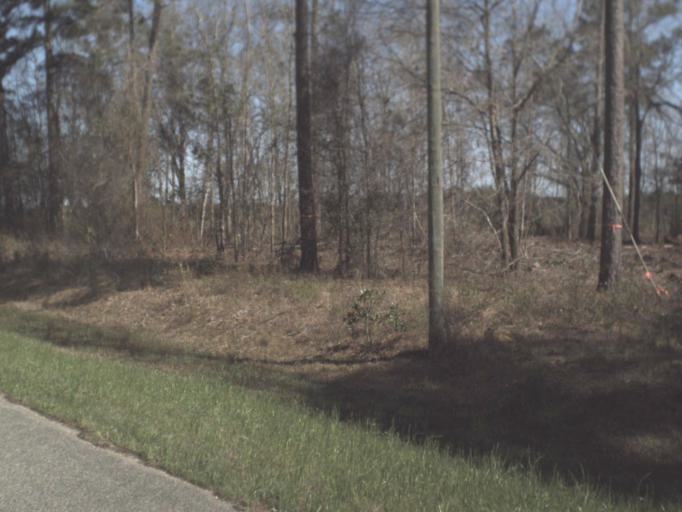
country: US
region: Florida
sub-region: Calhoun County
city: Blountstown
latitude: 30.5609
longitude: -85.0216
